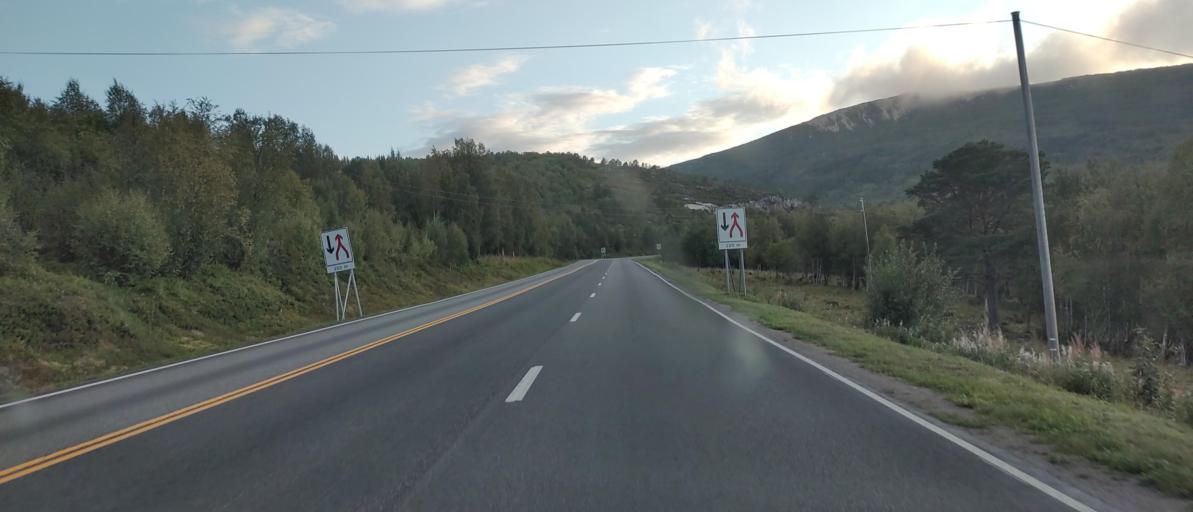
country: NO
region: Nordland
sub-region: Lodingen
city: Lodingen
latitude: 68.2188
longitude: 16.0683
